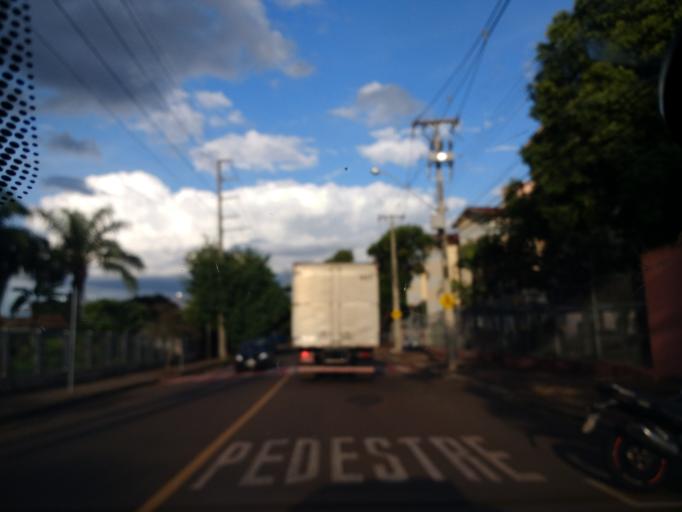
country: BR
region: Parana
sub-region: Londrina
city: Londrina
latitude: -23.2952
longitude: -51.1683
